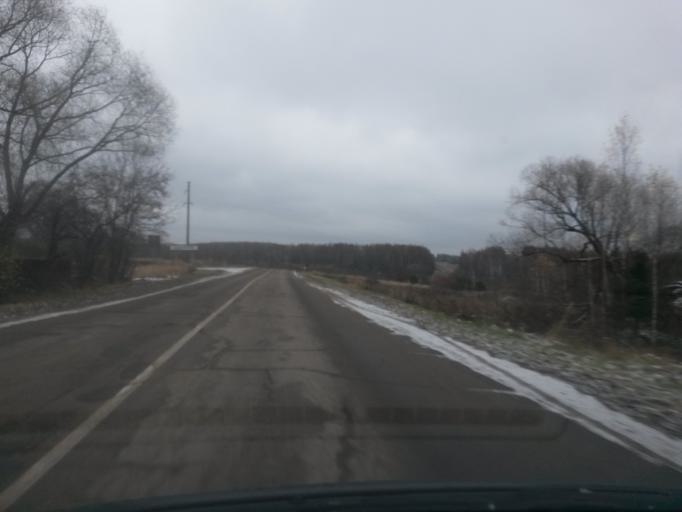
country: RU
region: Jaroslavl
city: Petrovsk
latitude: 56.9656
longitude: 39.3061
